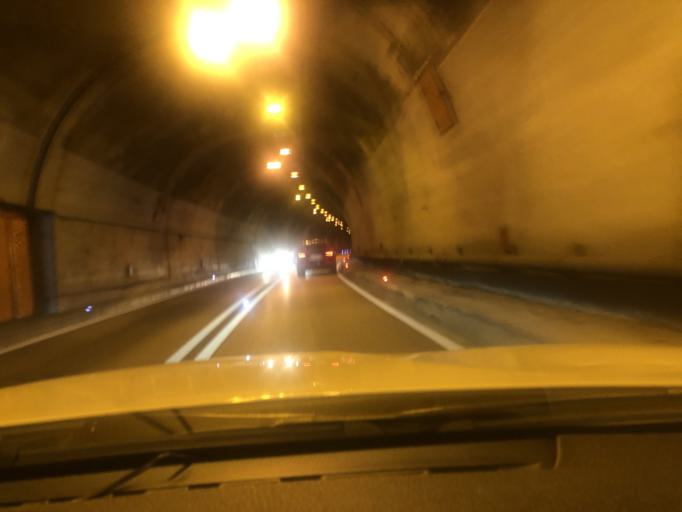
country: HR
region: Splitsko-Dalmatinska
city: Stari Grad
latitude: 43.1651
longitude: 16.5562
